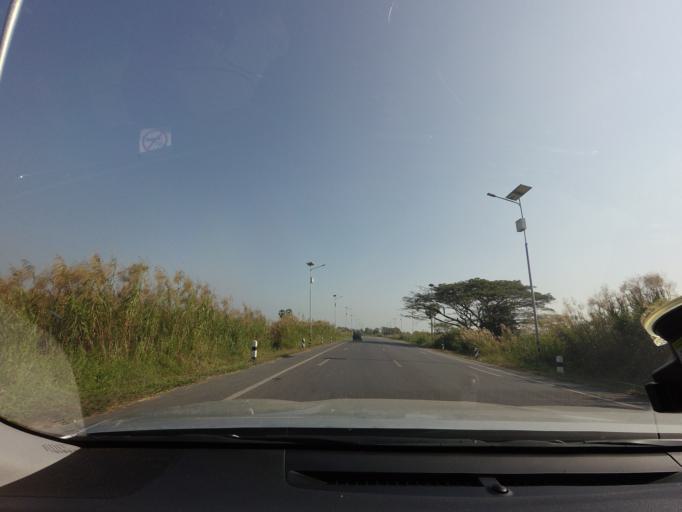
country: TH
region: Nakhon Si Thammarat
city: Nakhon Si Thammarat
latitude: 8.4654
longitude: 99.9801
